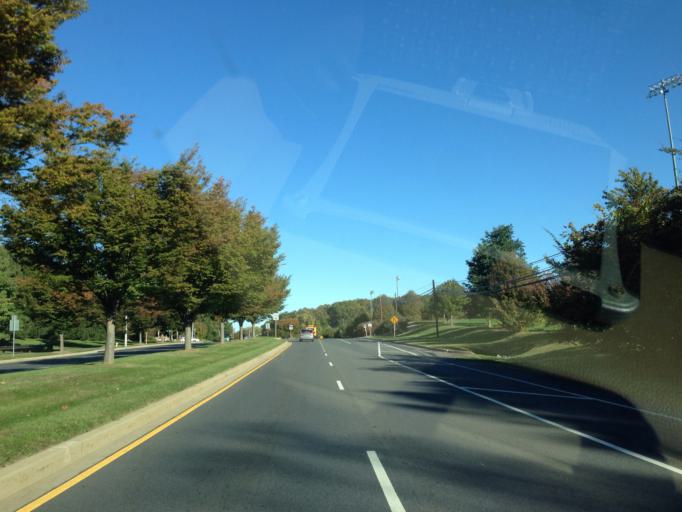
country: US
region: Maryland
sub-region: Montgomery County
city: Germantown
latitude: 39.2074
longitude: -77.2467
